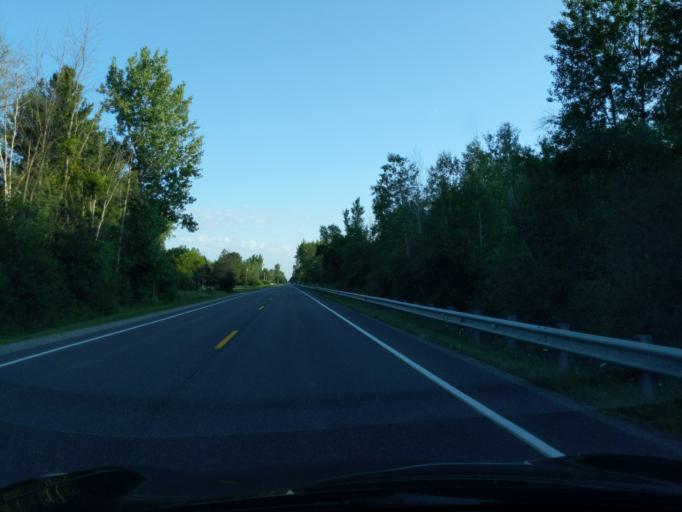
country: US
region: Michigan
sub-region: Midland County
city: Midland
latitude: 43.5524
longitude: -84.3697
